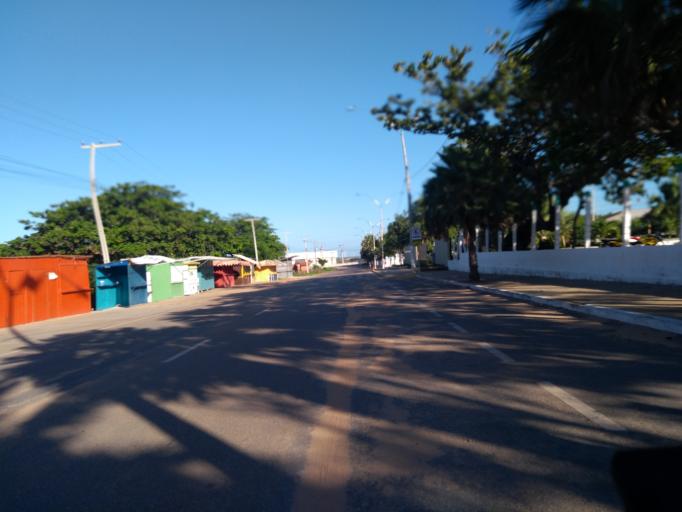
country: BR
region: Ceara
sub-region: Aracati
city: Aracati
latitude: -4.5711
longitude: -37.7935
